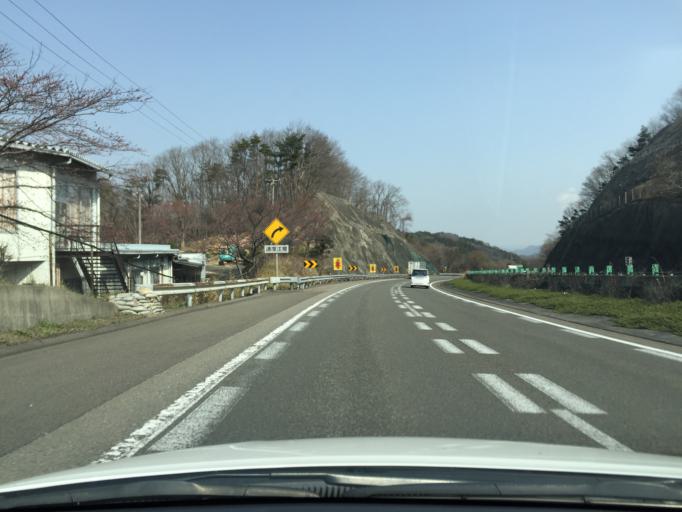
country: JP
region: Miyagi
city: Shiroishi
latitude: 37.9428
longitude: 140.6120
